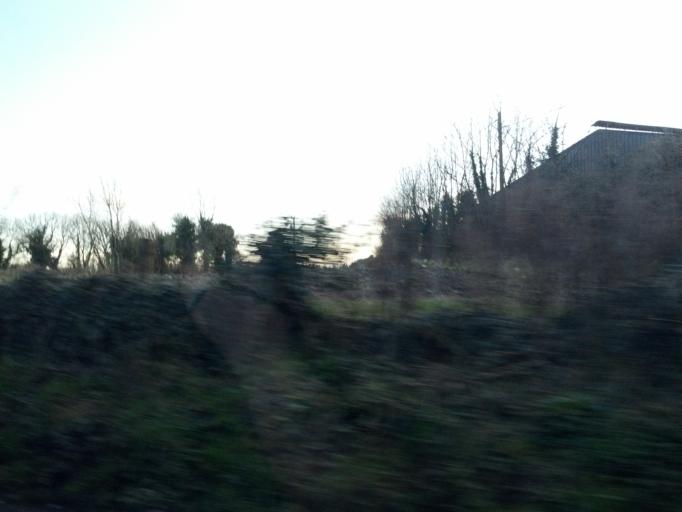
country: IE
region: Connaught
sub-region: County Galway
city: Athenry
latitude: 53.3261
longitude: -8.6243
